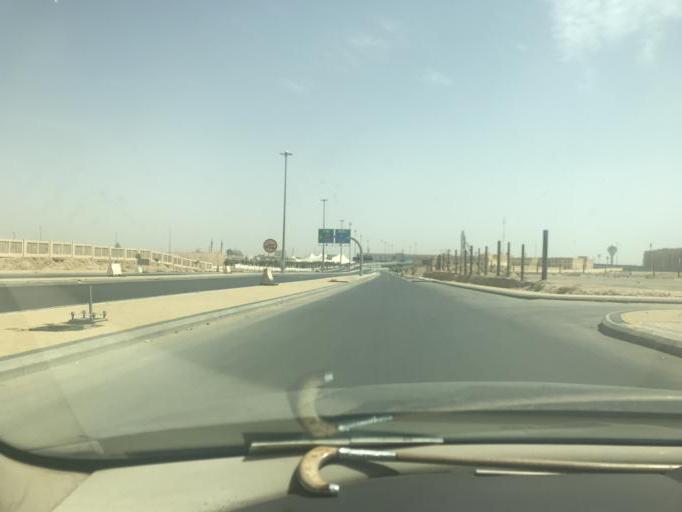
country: SA
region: Ar Riyad
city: Riyadh
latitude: 24.8259
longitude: 46.6966
